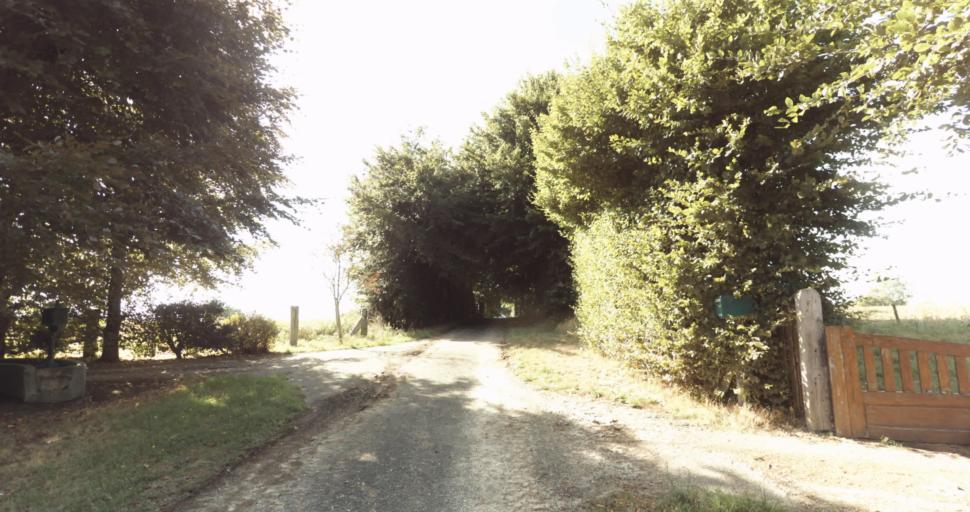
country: FR
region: Lower Normandy
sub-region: Departement de l'Orne
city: Vimoutiers
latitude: 48.9330
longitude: 0.1233
